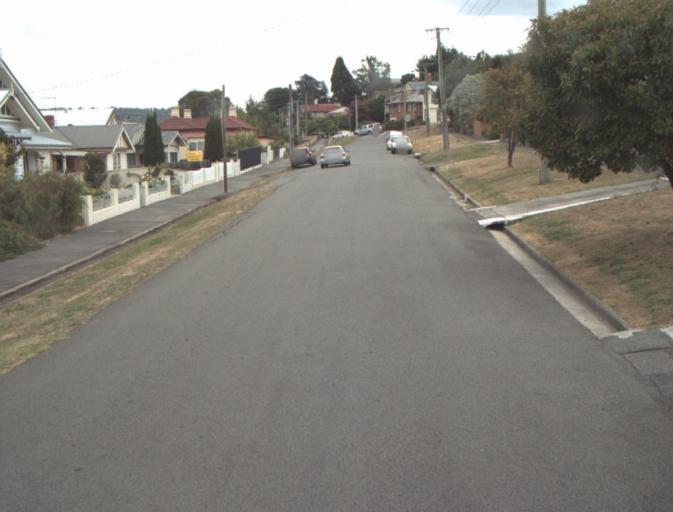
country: AU
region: Tasmania
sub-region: Launceston
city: Newnham
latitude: -41.4087
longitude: 147.1342
